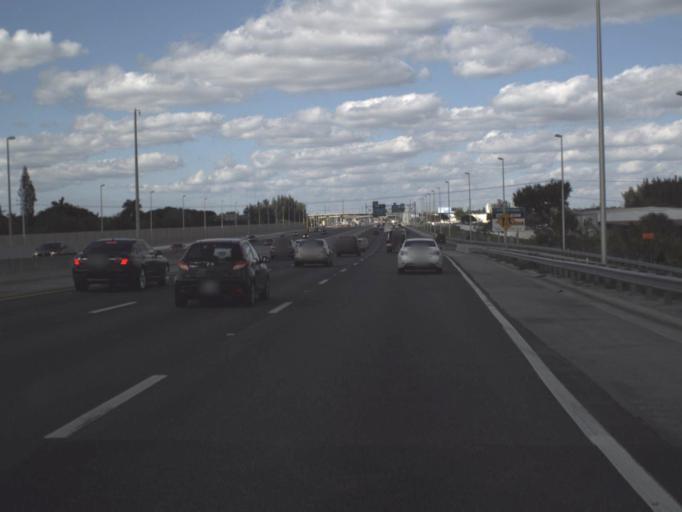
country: US
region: Florida
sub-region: Broward County
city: Davie
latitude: 26.0681
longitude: -80.2154
